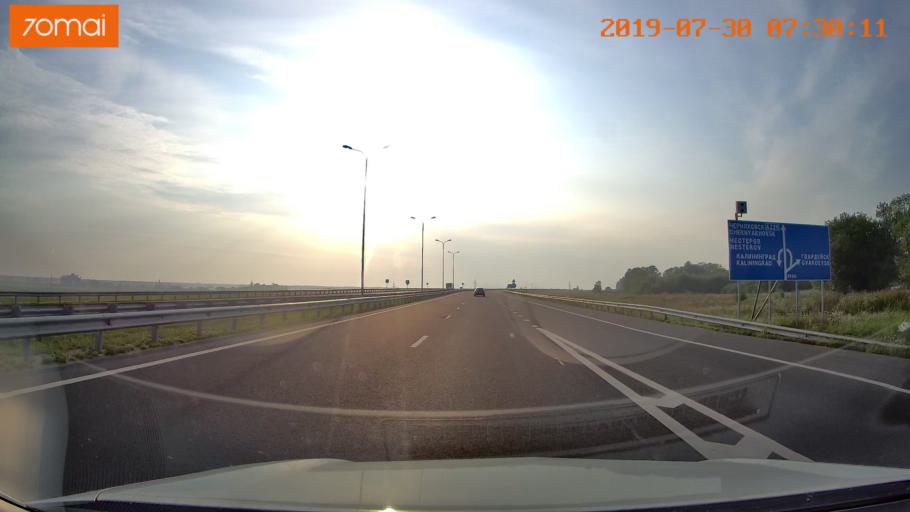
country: RU
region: Kaliningrad
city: Gvardeysk
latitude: 54.6704
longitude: 20.9582
